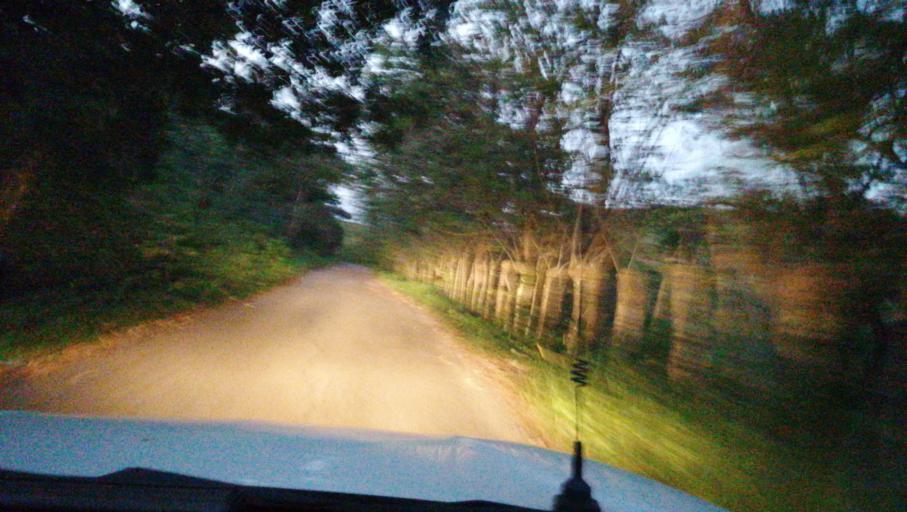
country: MX
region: Chiapas
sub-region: Ostuacan
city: Nuevo Juan del Grijalva
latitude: 17.4760
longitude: -93.3456
